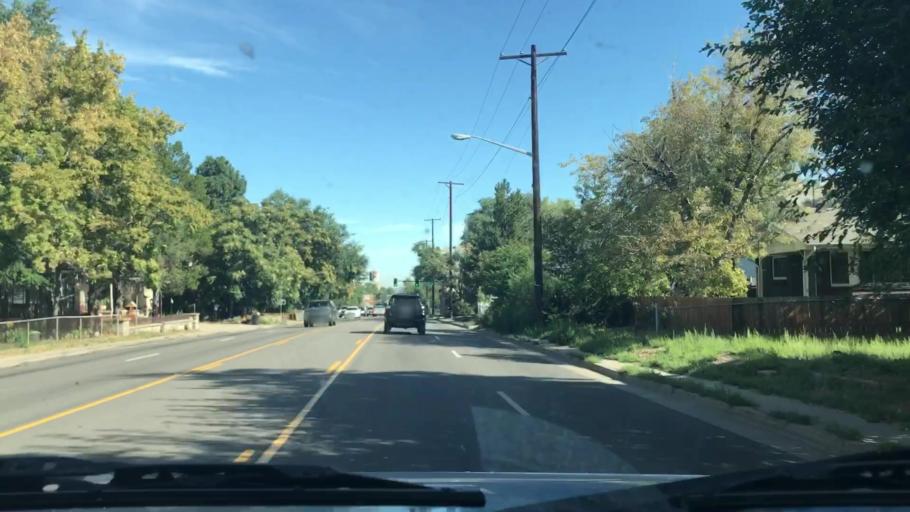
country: US
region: Colorado
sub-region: Jefferson County
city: Edgewater
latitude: 39.7715
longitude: -105.0532
